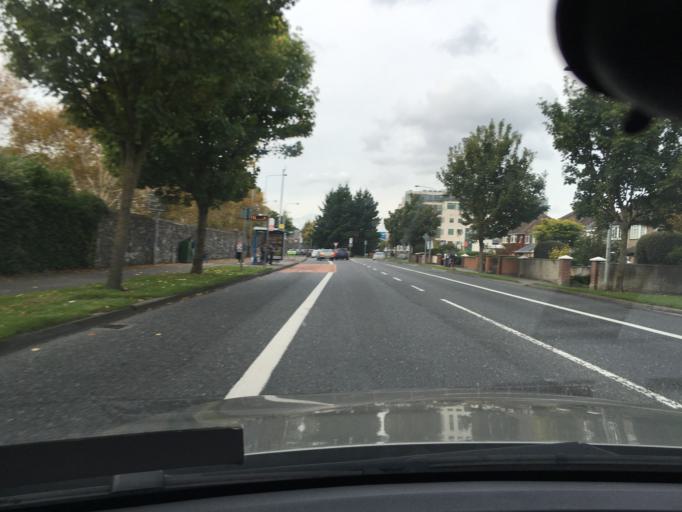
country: IE
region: Leinster
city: Chapelizod
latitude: 53.3714
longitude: -6.3299
